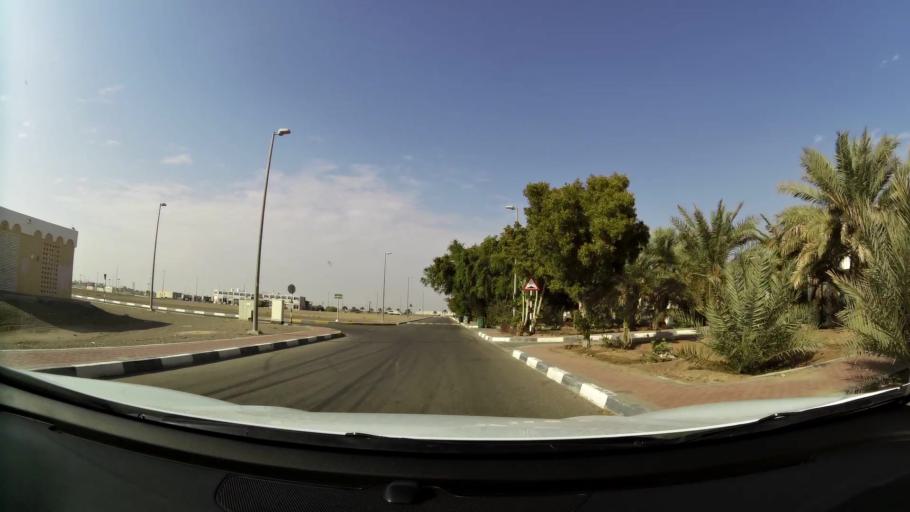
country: AE
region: Abu Dhabi
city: Al Ain
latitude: 24.0887
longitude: 55.8683
